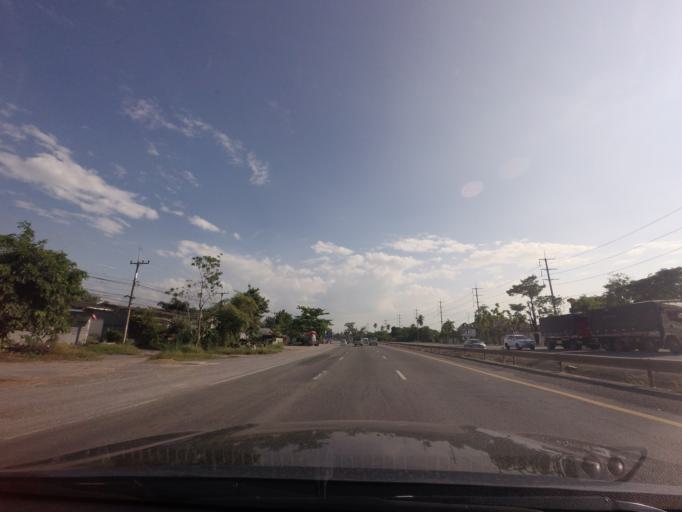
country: TH
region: Sara Buri
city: Chaloem Phra Kiat
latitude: 14.6523
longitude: 100.8844
